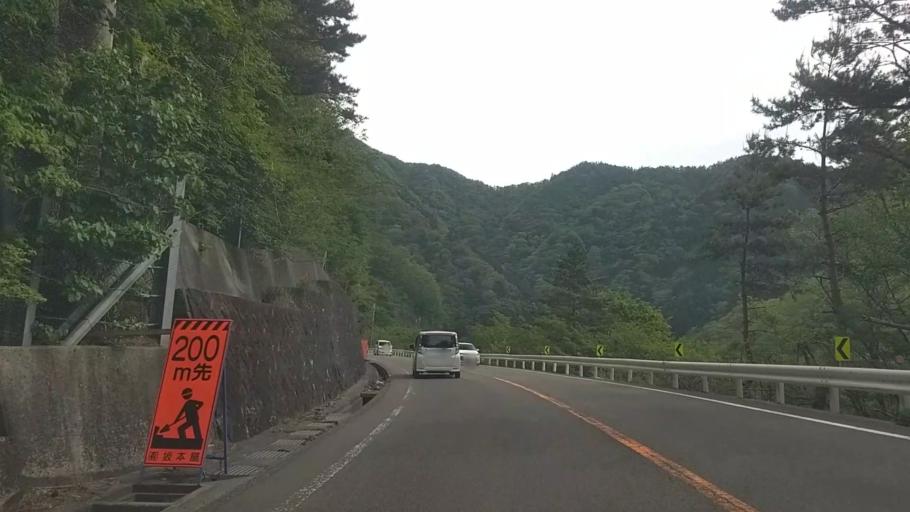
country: JP
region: Yamanashi
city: Fujikawaguchiko
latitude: 35.5122
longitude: 138.6160
